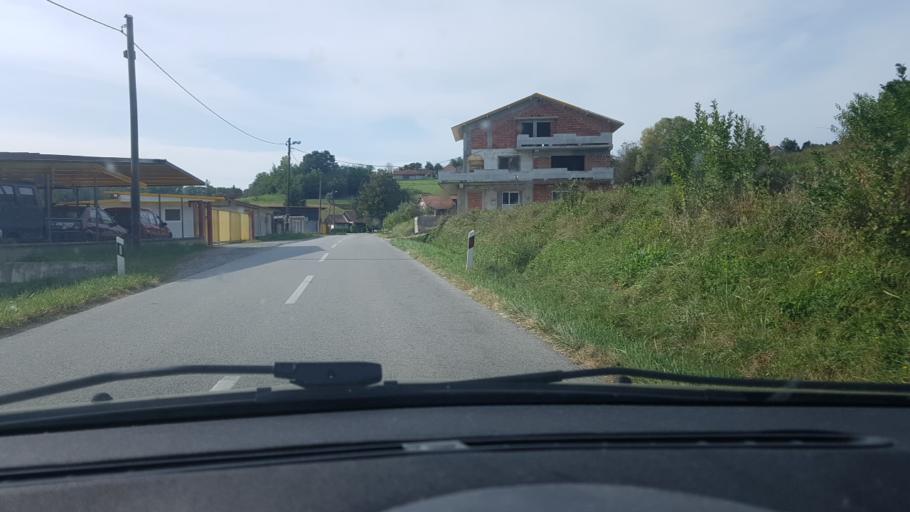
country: HR
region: Krapinsko-Zagorska
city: Mihovljan
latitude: 46.1278
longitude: 15.9769
